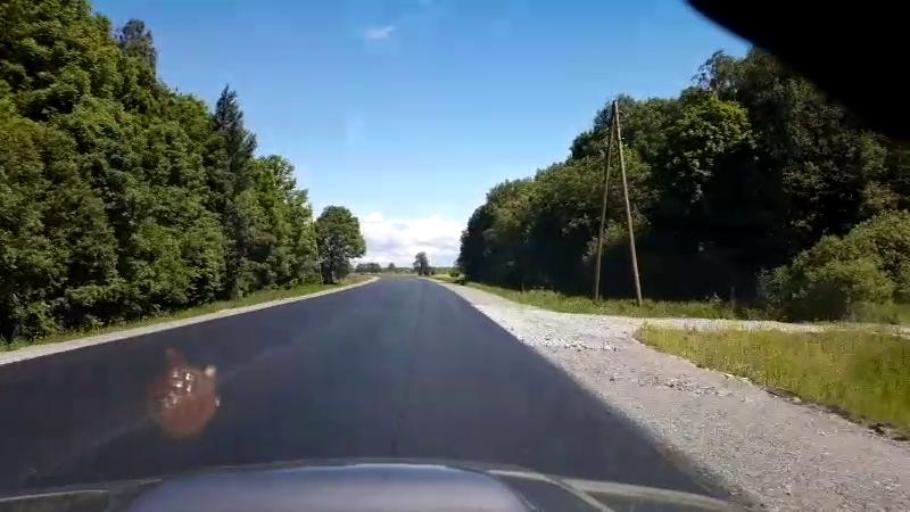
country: LV
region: Salacgrivas
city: Ainazi
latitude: 57.8538
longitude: 24.3614
